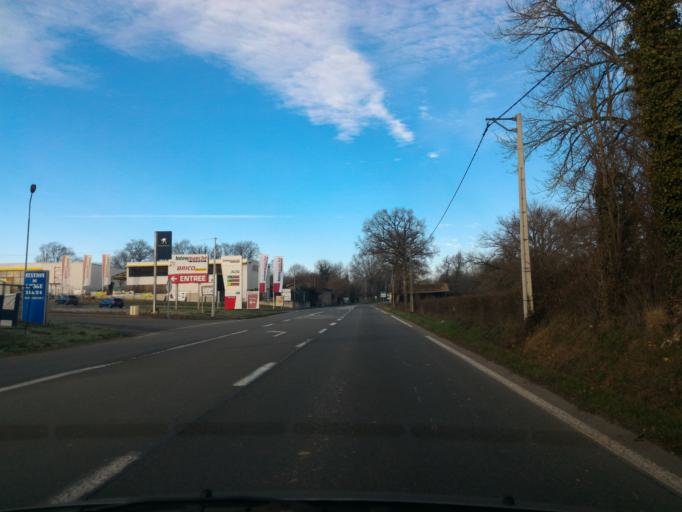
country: FR
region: Poitou-Charentes
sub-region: Departement de la Charente
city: Confolens
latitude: 46.0214
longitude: 0.6576
